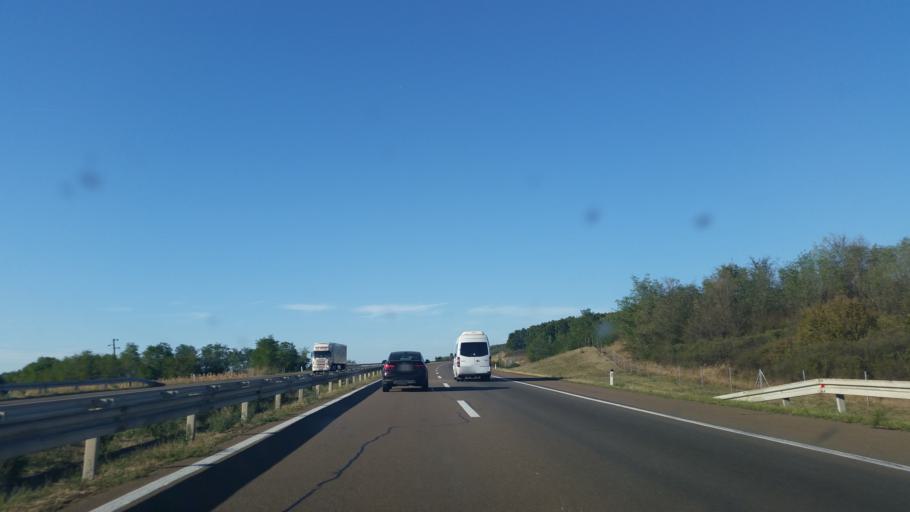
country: RS
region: Central Serbia
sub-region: Pomoravski Okrug
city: Paracin
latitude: 43.8165
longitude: 21.4274
